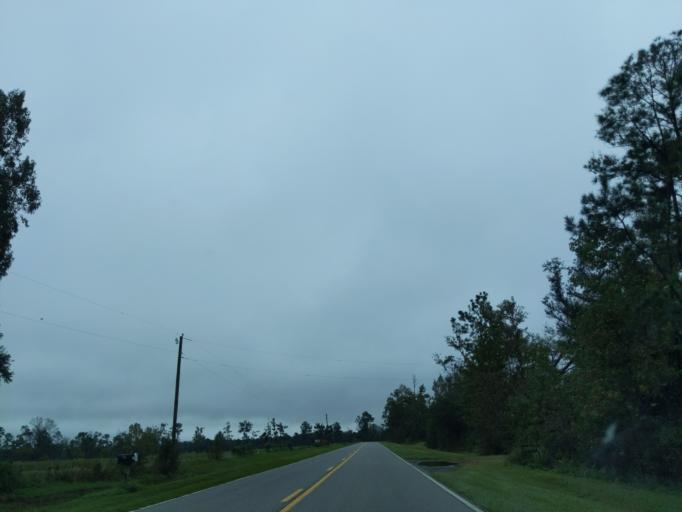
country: US
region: Florida
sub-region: Jackson County
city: Sneads
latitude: 30.6608
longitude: -84.9354
